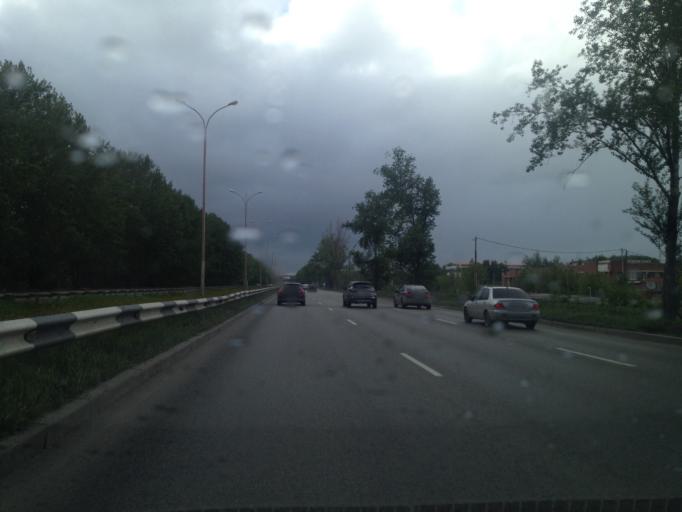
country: RU
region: Sverdlovsk
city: Sovkhoznyy
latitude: 56.7948
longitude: 60.5647
